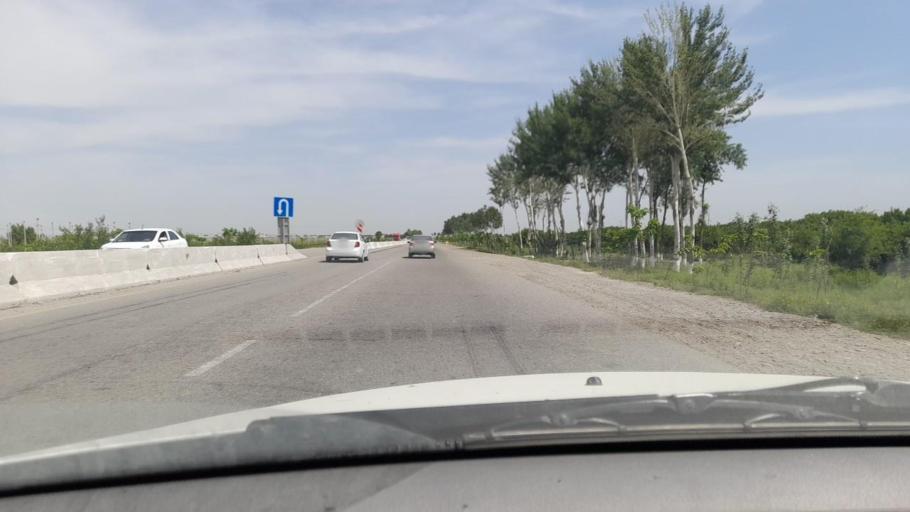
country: UZ
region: Bukhara
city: Galaosiyo
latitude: 39.8880
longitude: 64.4650
